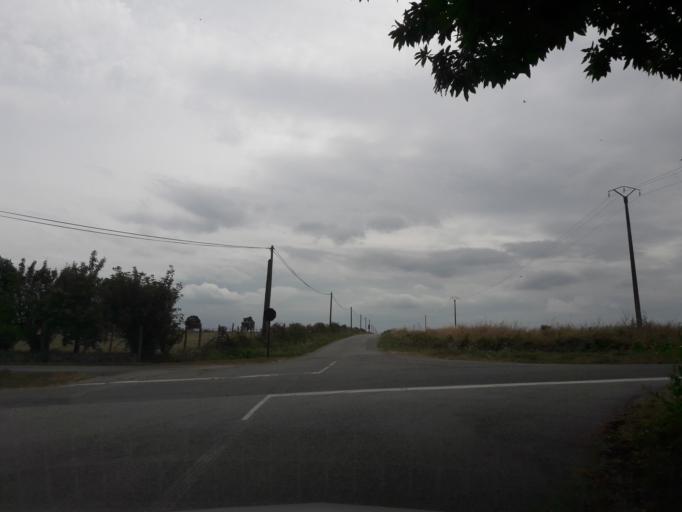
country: FR
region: Brittany
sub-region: Departement d'Ille-et-Vilaine
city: Bain-de-Bretagne
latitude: 47.8460
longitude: -1.6692
